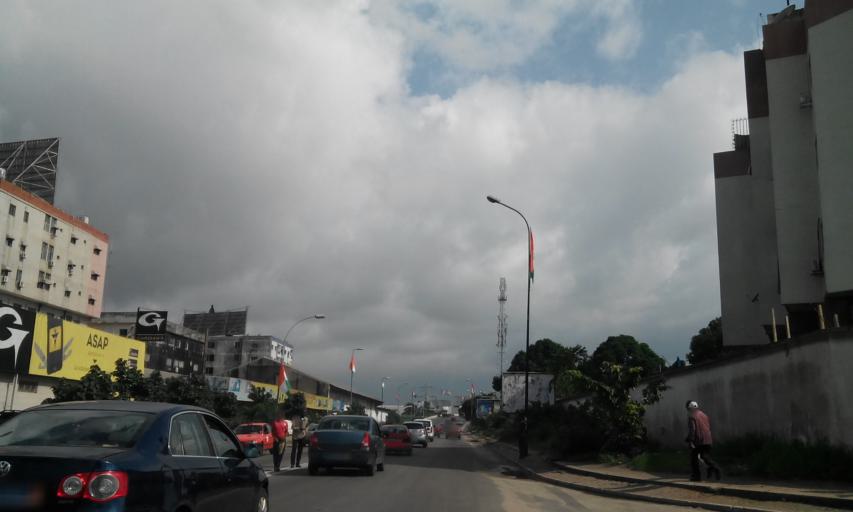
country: CI
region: Lagunes
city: Abidjan
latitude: 5.3055
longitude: -4.0166
